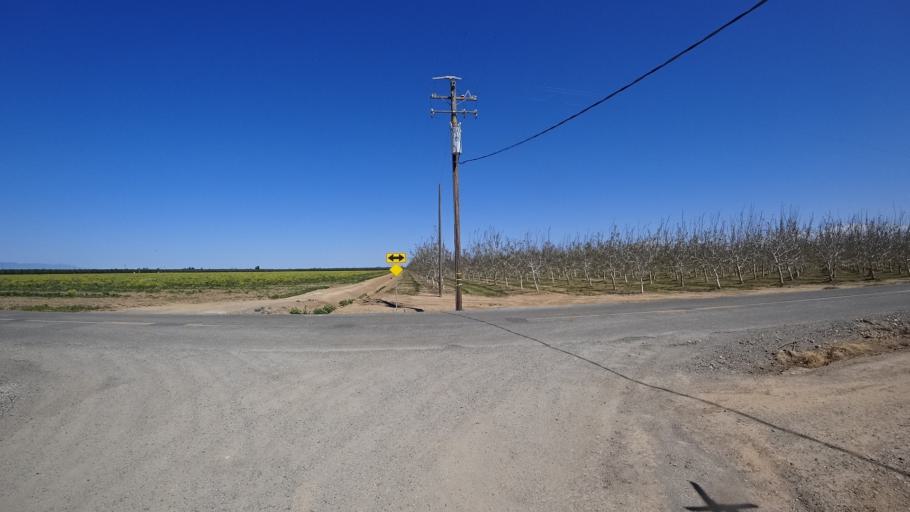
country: US
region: California
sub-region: Glenn County
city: Orland
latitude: 39.6963
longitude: -122.1591
